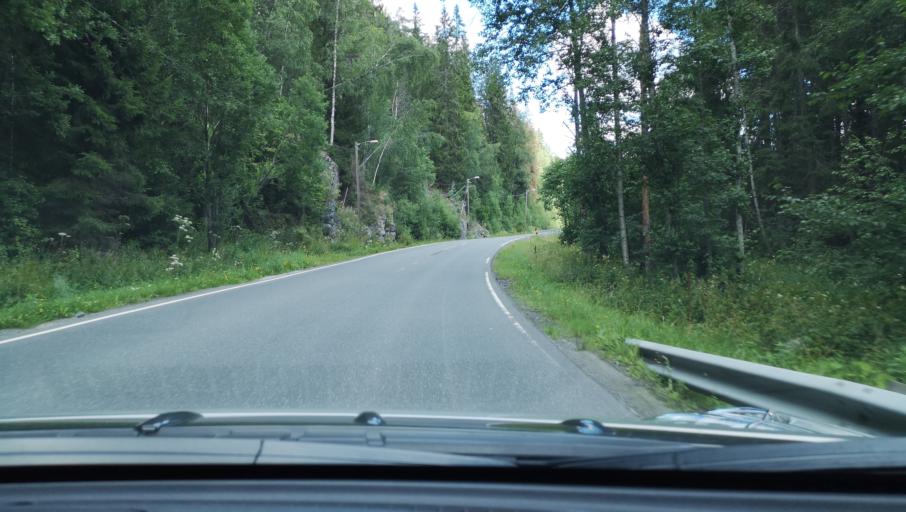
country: NO
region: Ostfold
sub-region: Hobol
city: Tomter
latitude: 59.6496
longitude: 10.9919
